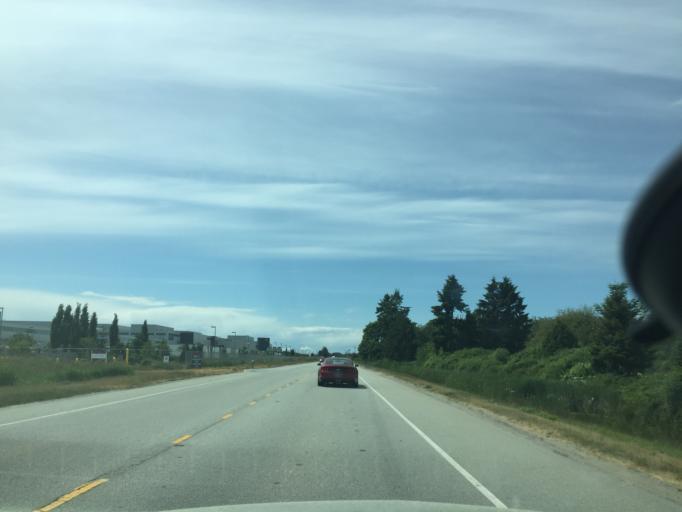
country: CA
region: British Columbia
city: Richmond
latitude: 49.2057
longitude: -123.1628
